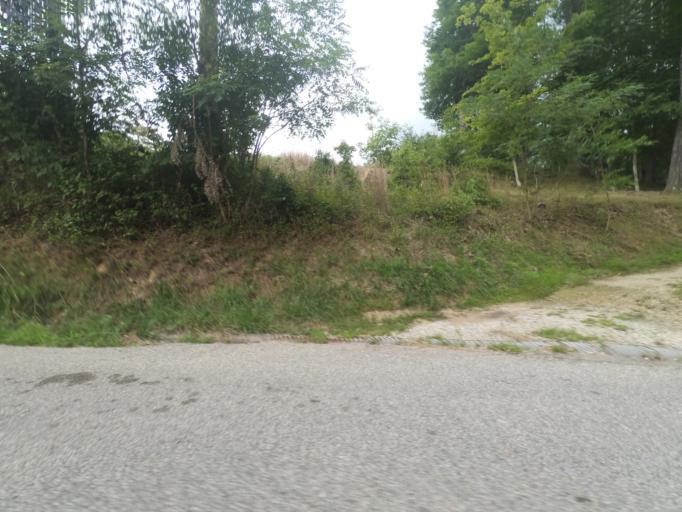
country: US
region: West Virginia
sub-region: Cabell County
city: Huntington
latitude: 38.3843
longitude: -82.4135
